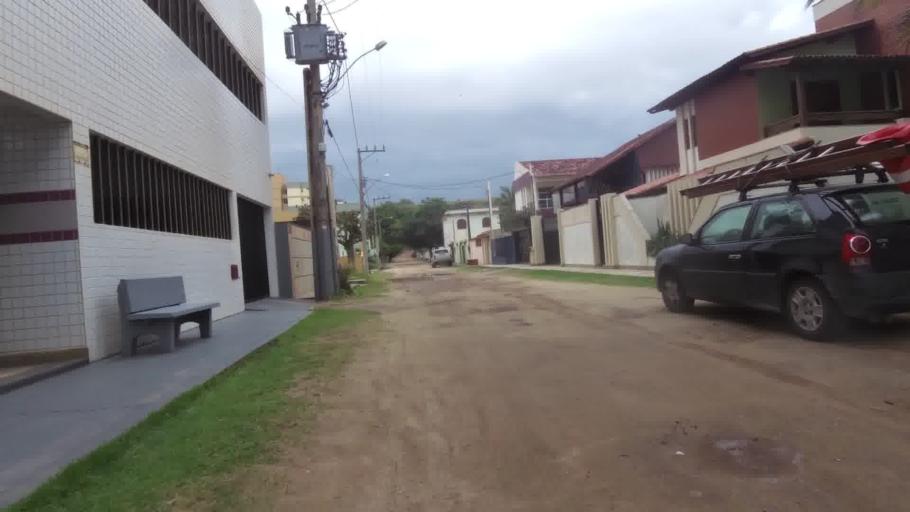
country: BR
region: Espirito Santo
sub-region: Marataizes
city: Marataizes
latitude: -21.0539
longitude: -40.8329
